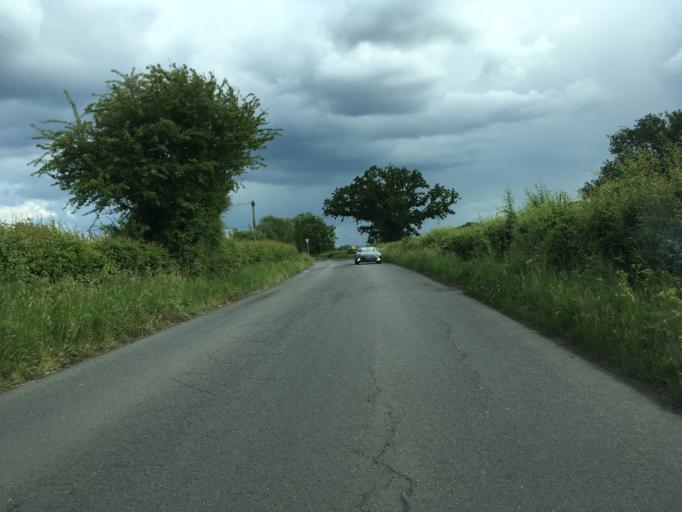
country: GB
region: England
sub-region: Wiltshire
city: Purton
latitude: 51.6069
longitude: -1.8486
